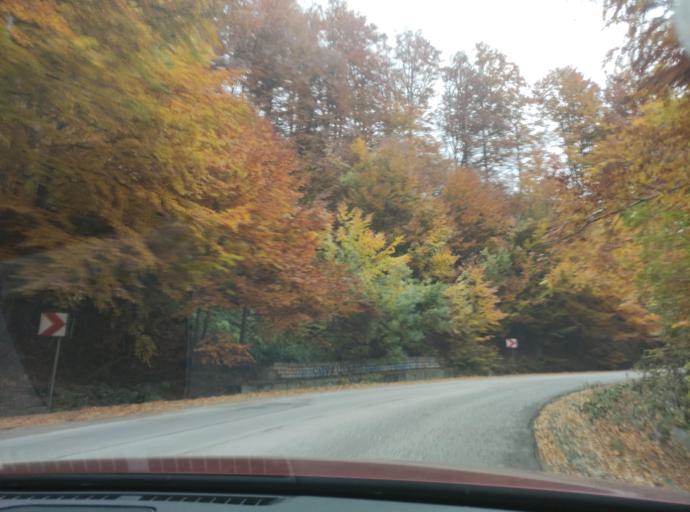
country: BG
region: Montana
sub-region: Obshtina Berkovitsa
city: Berkovitsa
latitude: 43.1193
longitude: 23.1186
